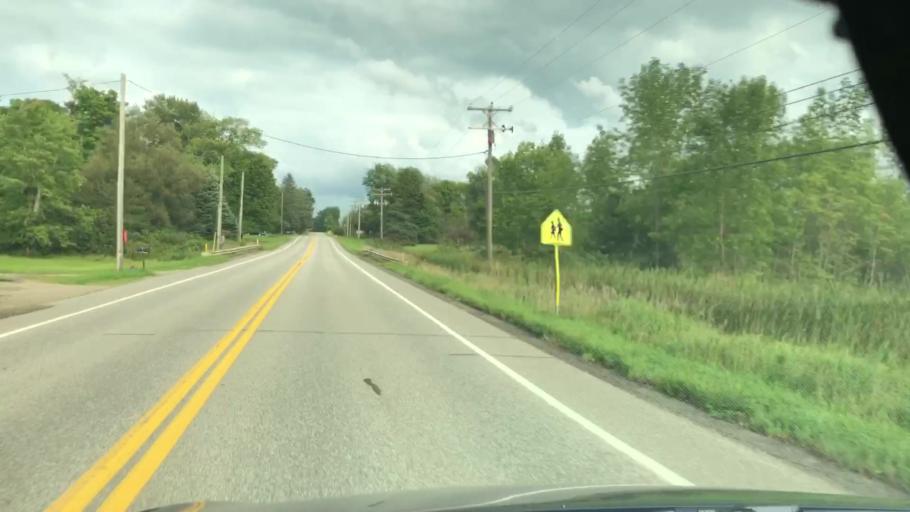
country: US
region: Pennsylvania
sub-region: Erie County
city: Northwest Harborcreek
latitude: 42.0573
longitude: -79.9095
